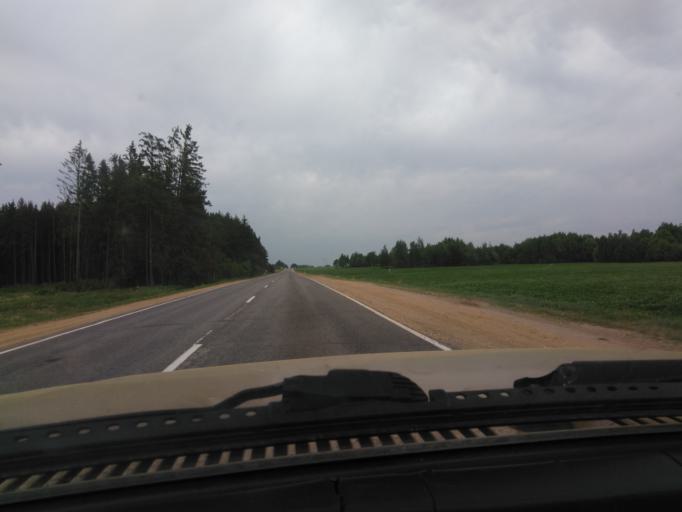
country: BY
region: Mogilev
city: Kamyennyya Lavy
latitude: 54.0454
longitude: 30.3253
